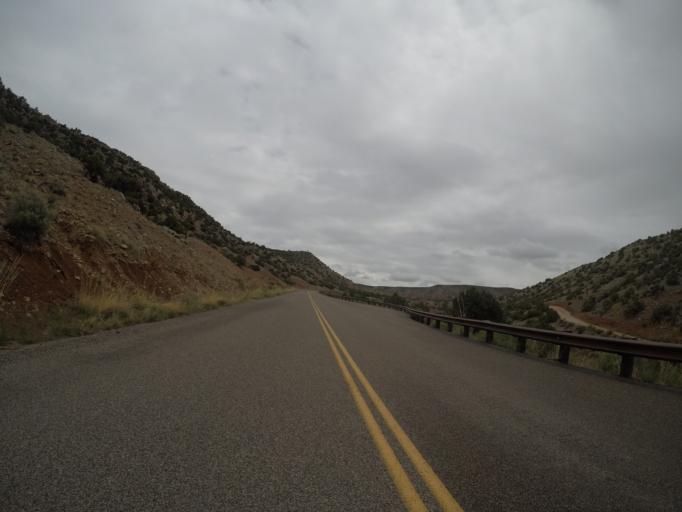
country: US
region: Wyoming
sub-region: Big Horn County
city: Lovell
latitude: 45.1017
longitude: -108.2208
